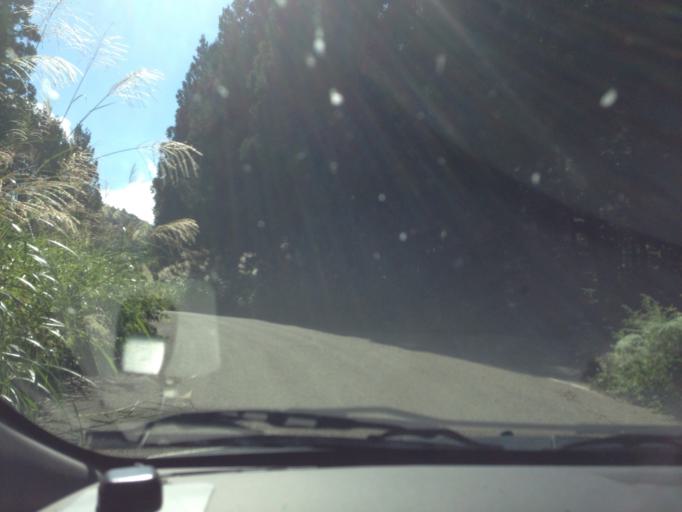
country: JP
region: Fukushima
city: Kitakata
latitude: 37.4292
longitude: 139.7885
